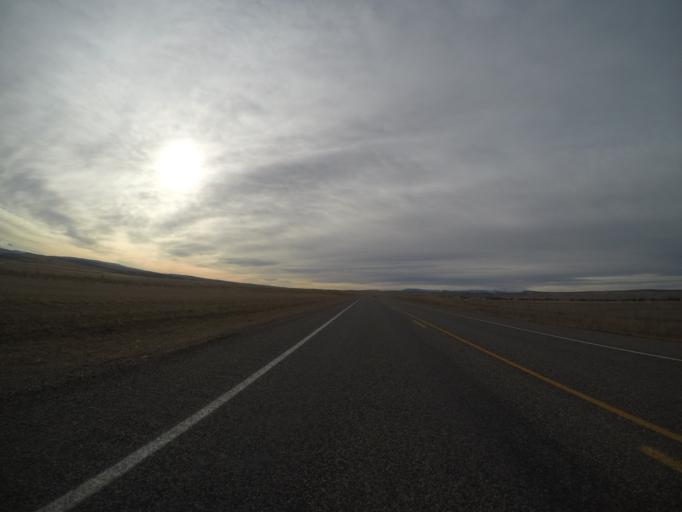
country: US
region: Montana
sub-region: Yellowstone County
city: Laurel
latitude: 45.5772
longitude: -108.8443
